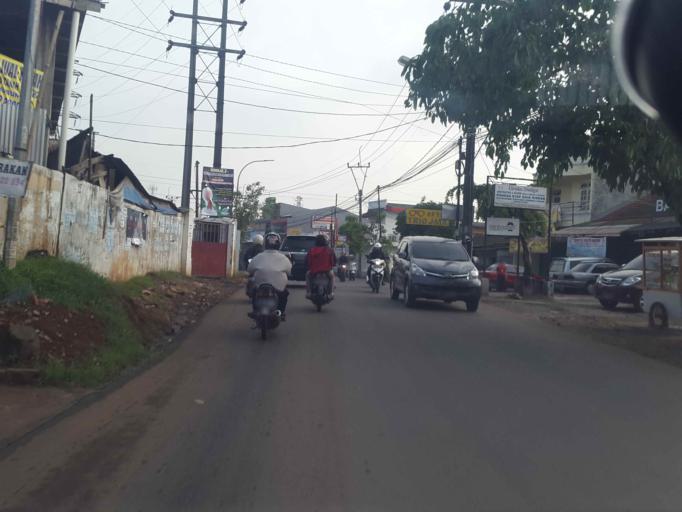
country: ID
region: West Java
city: Bekasi
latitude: -6.2859
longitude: 107.0352
